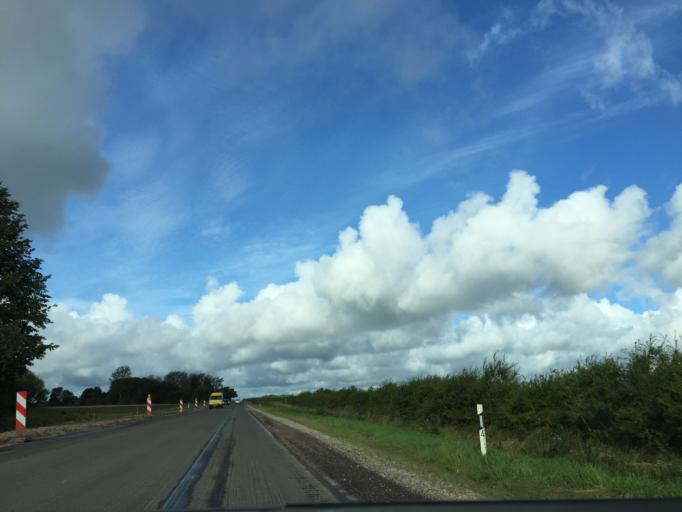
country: LV
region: Engure
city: Smarde
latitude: 56.9213
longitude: 23.2538
